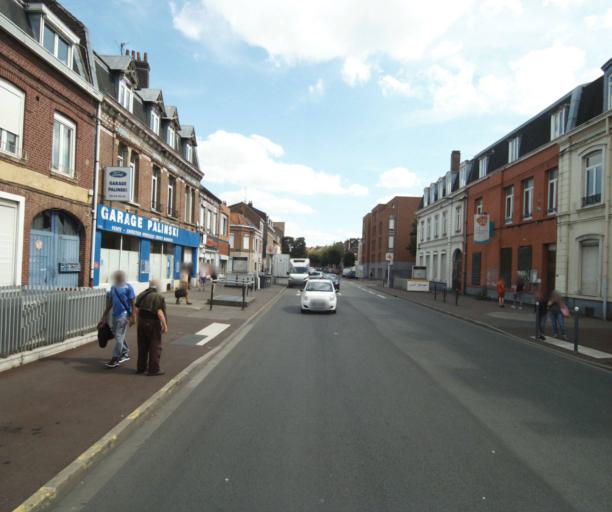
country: FR
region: Nord-Pas-de-Calais
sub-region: Departement du Nord
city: Mons-en-Baroeul
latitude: 50.6303
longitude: 3.0974
